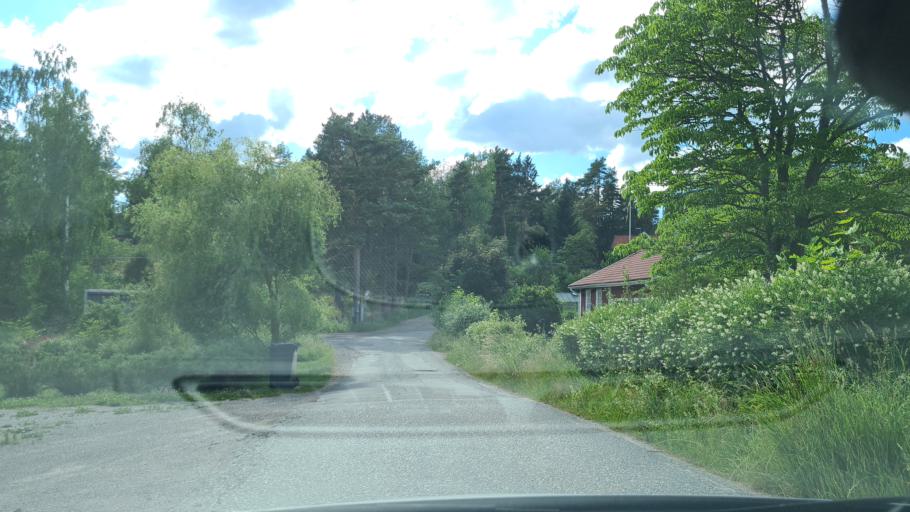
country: SE
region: Stockholm
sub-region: Vaxholms Kommun
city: Vaxholm
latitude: 59.4089
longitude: 18.3911
